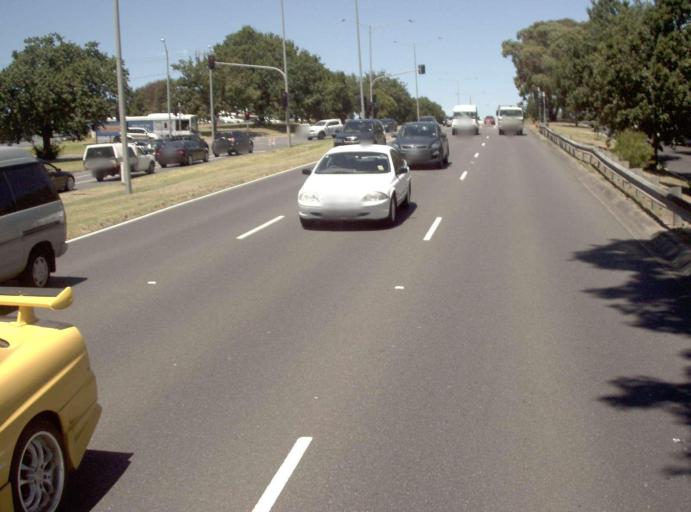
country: AU
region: Victoria
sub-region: Casey
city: Narre Warren
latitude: -38.0216
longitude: 145.2999
